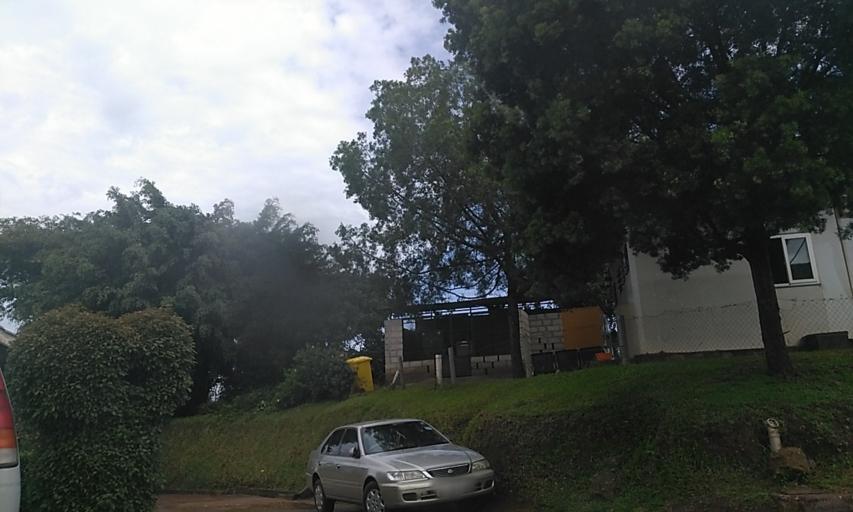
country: UG
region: Central Region
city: Kampala Central Division
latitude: 0.3327
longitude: 32.5850
